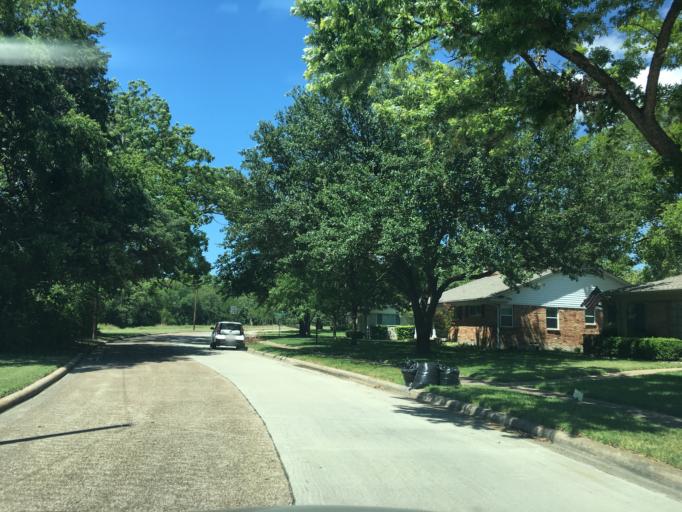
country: US
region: Texas
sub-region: Dallas County
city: Highland Park
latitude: 32.8448
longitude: -96.7037
